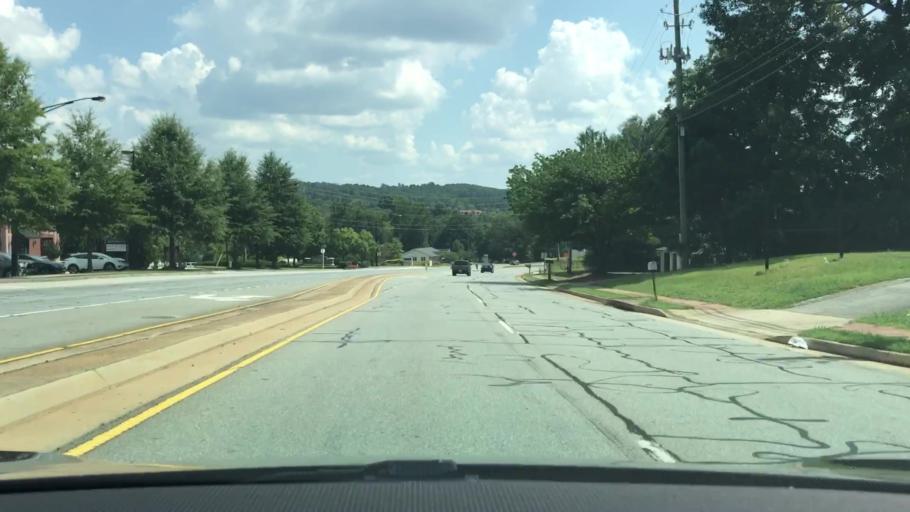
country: US
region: Georgia
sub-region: Gwinnett County
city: Buford
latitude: 34.0948
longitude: -83.9997
